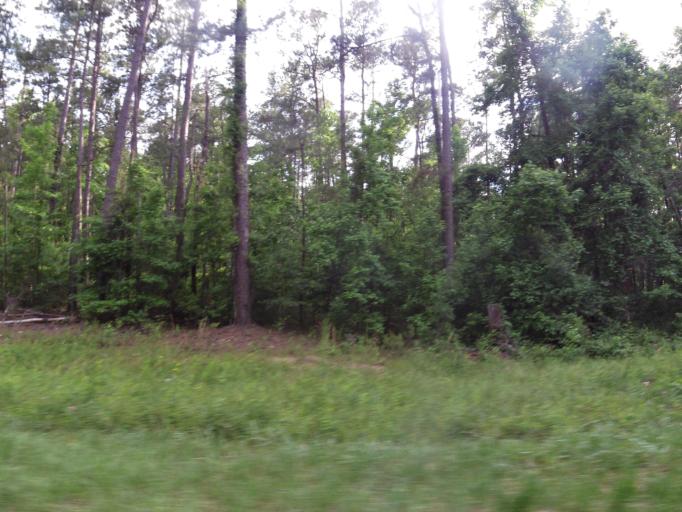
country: US
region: South Carolina
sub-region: Jasper County
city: Ridgeland
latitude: 32.5517
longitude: -81.1673
